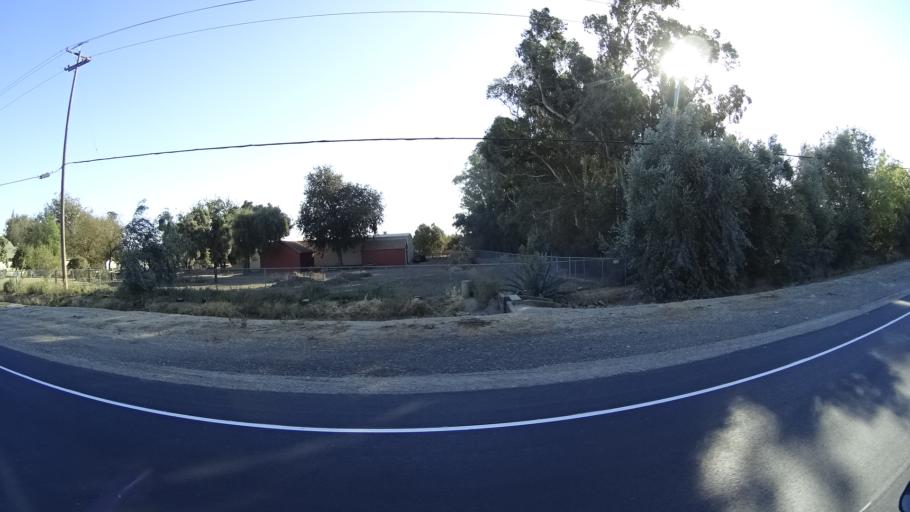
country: US
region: California
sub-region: Yolo County
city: Woodland
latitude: 38.6284
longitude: -121.7850
